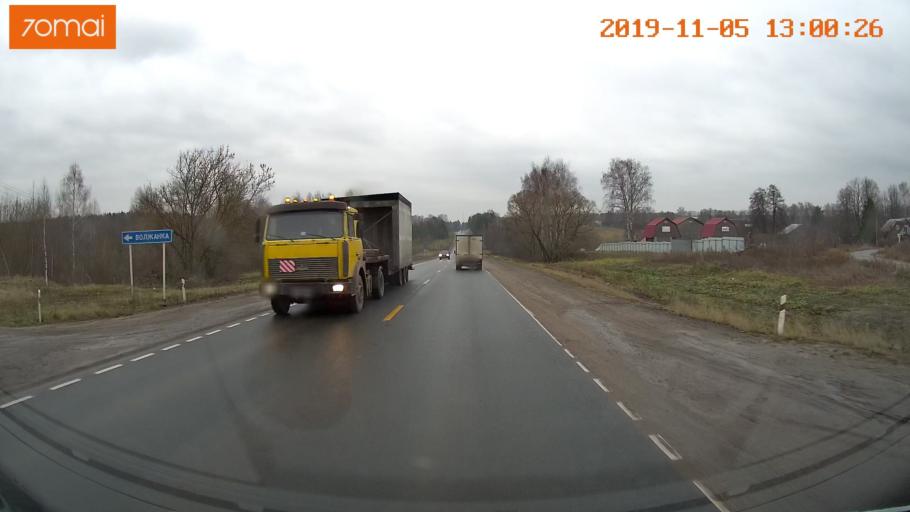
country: RU
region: Ivanovo
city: Kokhma
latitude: 56.9140
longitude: 41.1448
